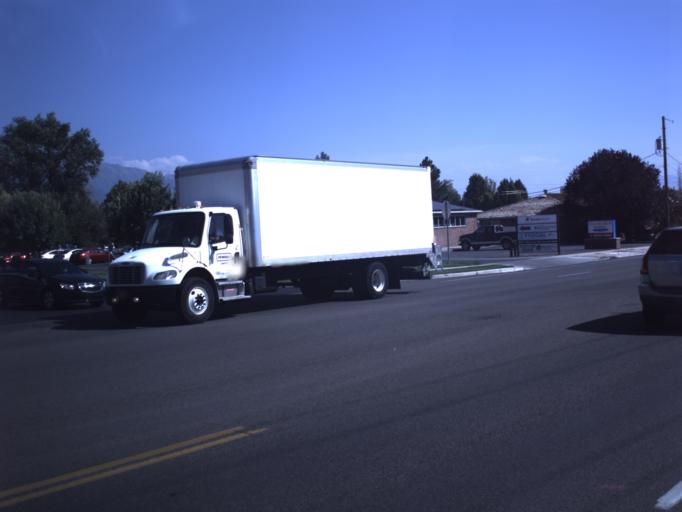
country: US
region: Utah
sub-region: Utah County
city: American Fork
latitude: 40.3787
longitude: -111.7692
